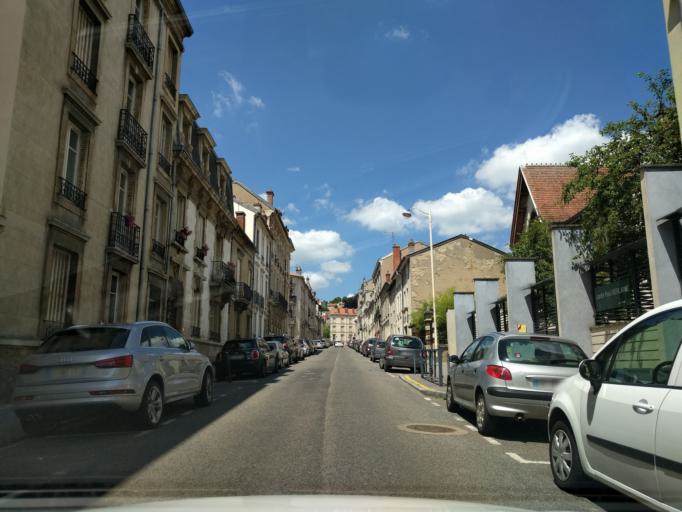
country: FR
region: Lorraine
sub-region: Departement de Meurthe-et-Moselle
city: Laxou
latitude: 48.6875
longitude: 6.1629
